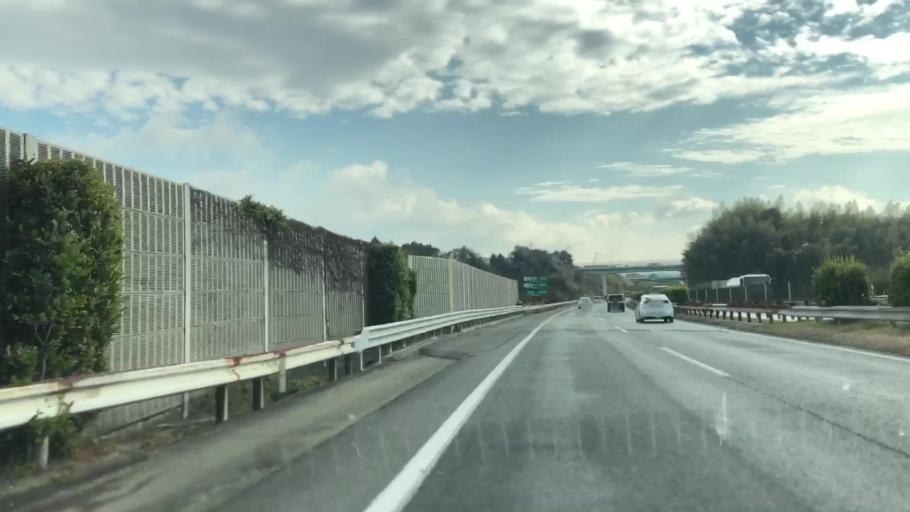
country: JP
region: Fukuoka
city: Setakamachi-takayanagi
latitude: 33.1356
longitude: 130.5160
